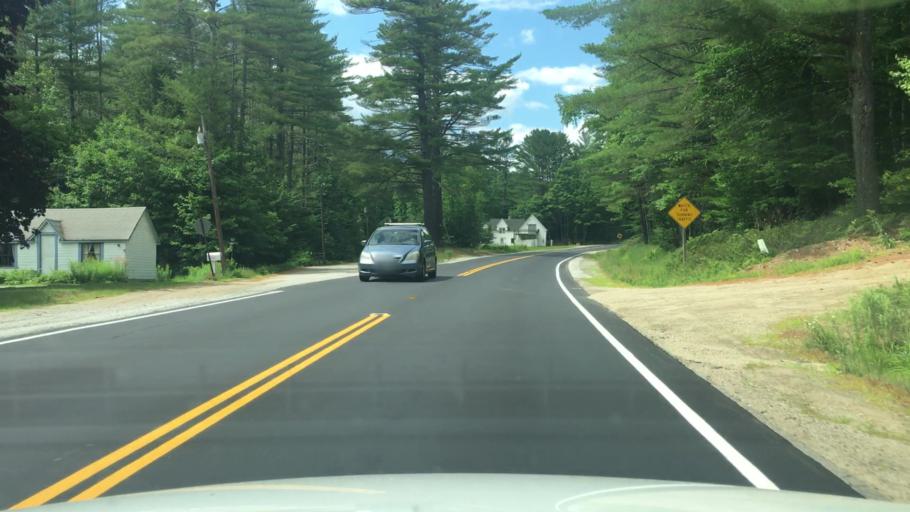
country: US
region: Maine
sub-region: Oxford County
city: West Paris
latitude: 44.3885
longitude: -70.6586
